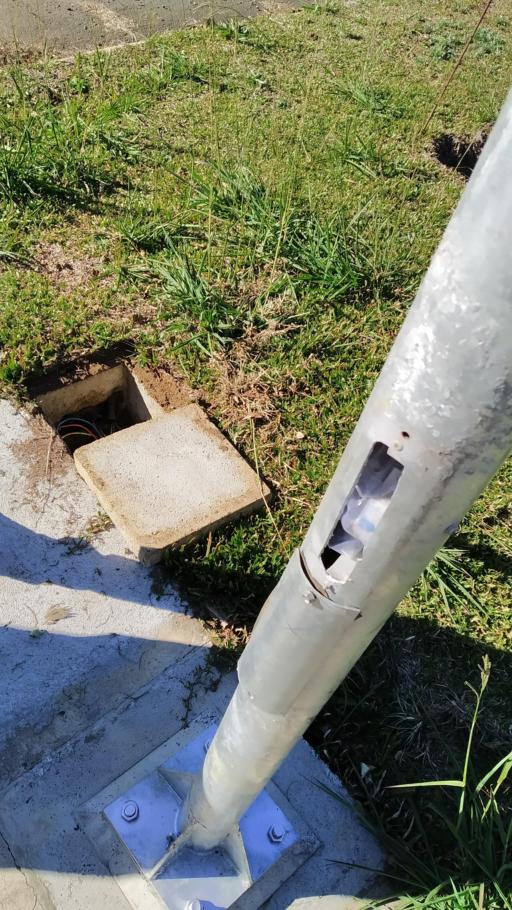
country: BR
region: Santa Catarina
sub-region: Curitibanos
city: Curitibanos
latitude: -27.2856
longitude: -50.5359
